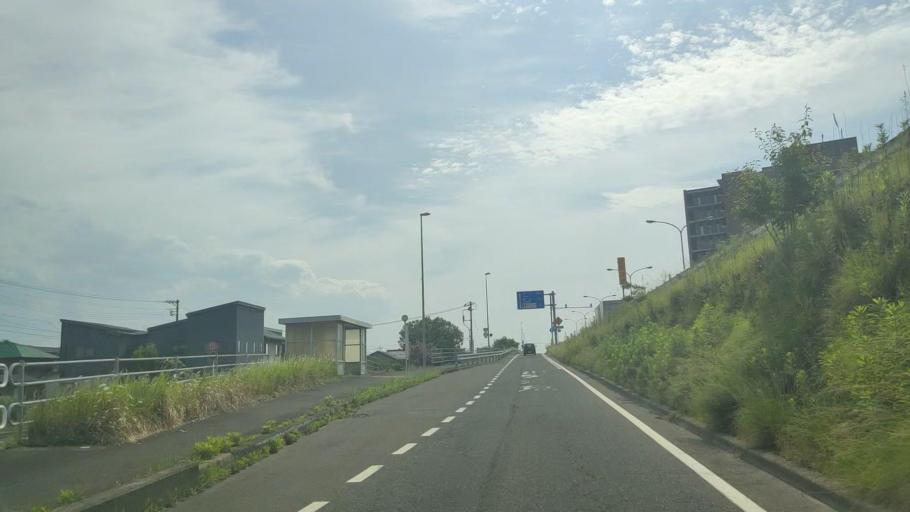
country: JP
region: Tottori
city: Tottori
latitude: 35.5214
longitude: 134.2147
